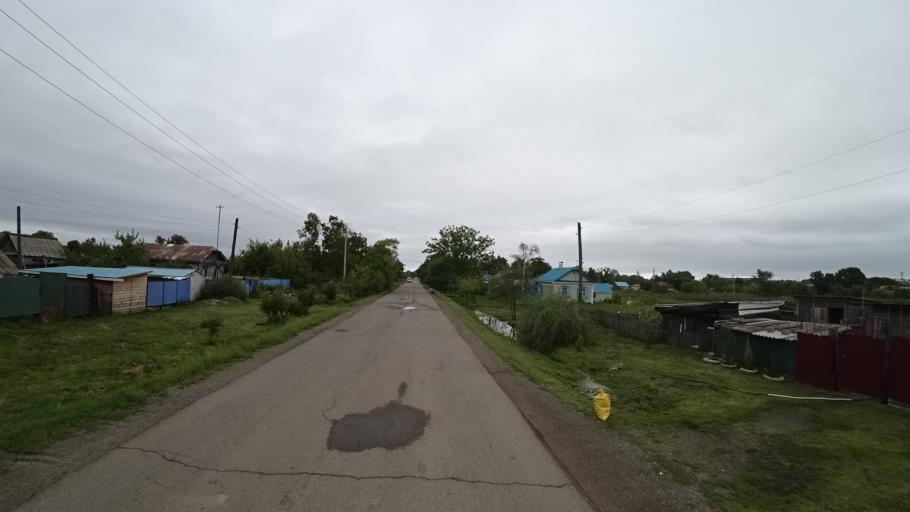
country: RU
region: Primorskiy
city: Chernigovka
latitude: 44.3475
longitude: 132.5639
